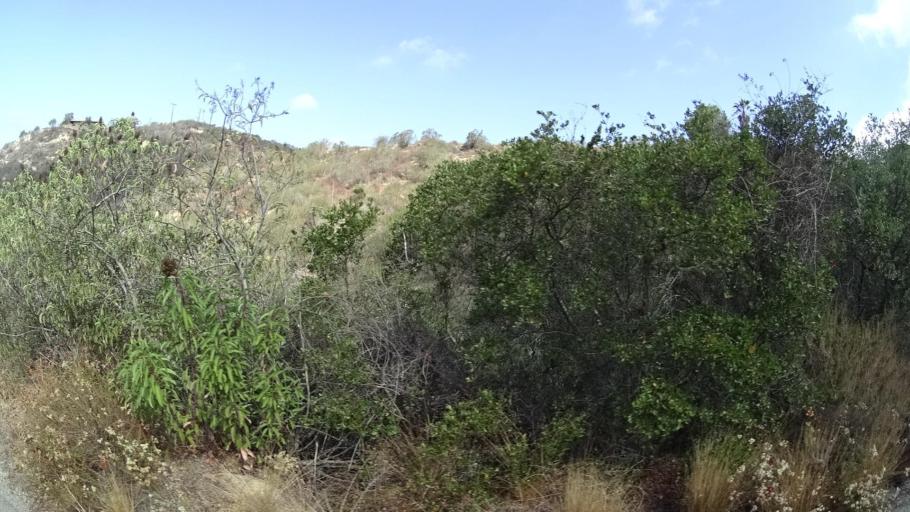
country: US
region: California
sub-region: San Diego County
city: Fallbrook
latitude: 33.4252
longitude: -117.2982
